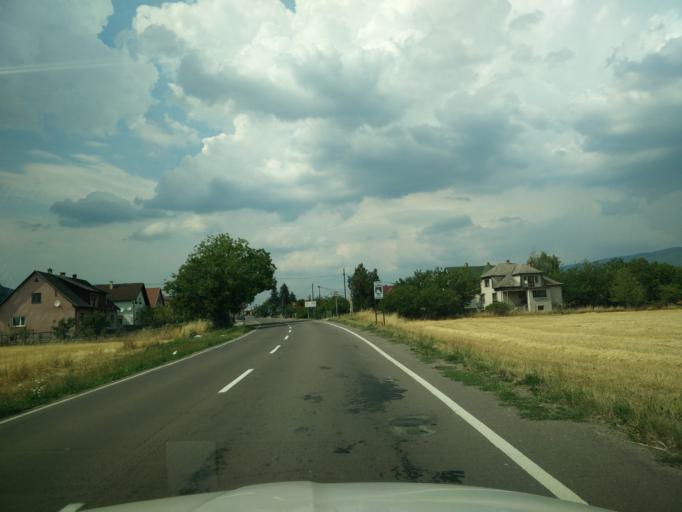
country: SK
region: Nitriansky
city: Novaky
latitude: 48.7616
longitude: 18.4964
